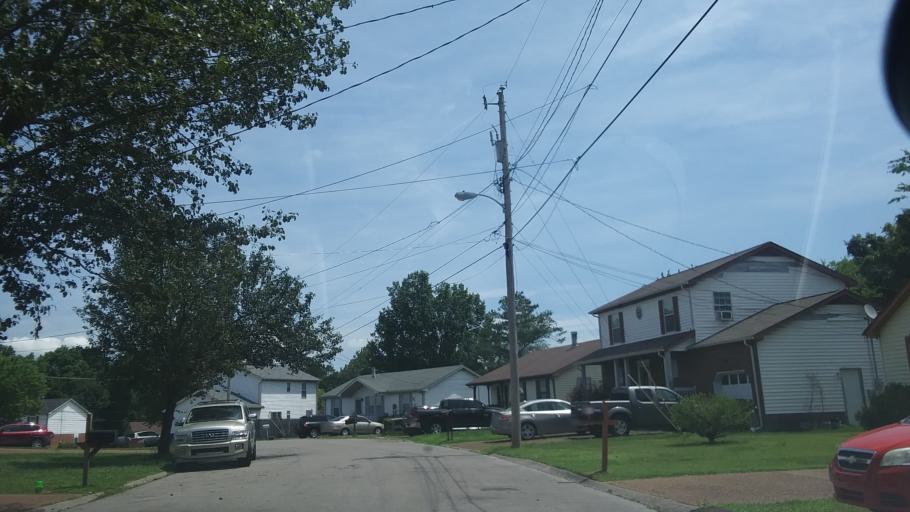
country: US
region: Tennessee
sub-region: Rutherford County
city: La Vergne
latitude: 36.0658
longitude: -86.6401
